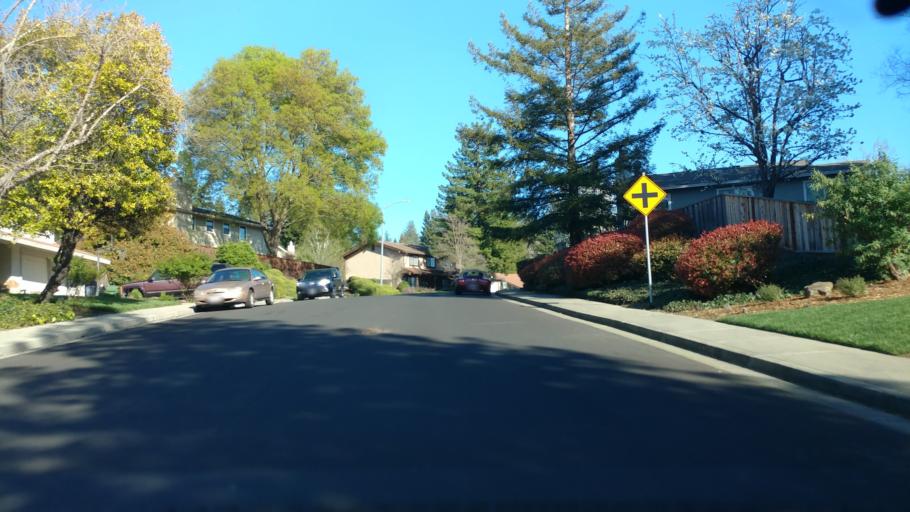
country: US
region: California
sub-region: Contra Costa County
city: San Ramon
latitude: 37.8037
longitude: -121.9740
